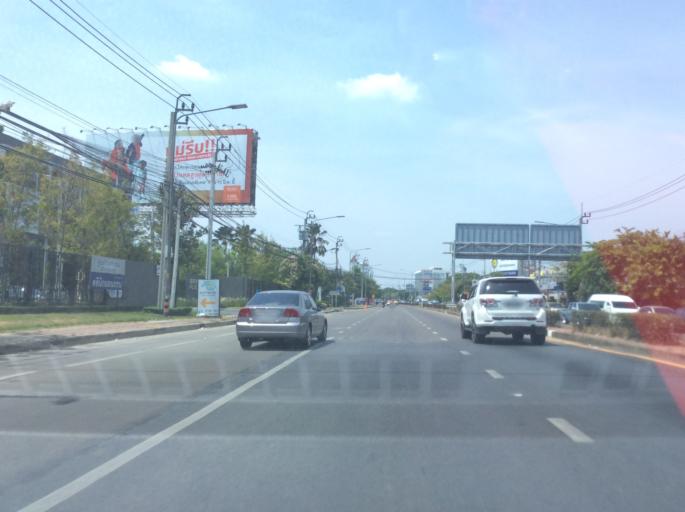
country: TH
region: Nonthaburi
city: Pak Kret
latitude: 13.9031
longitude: 100.5163
